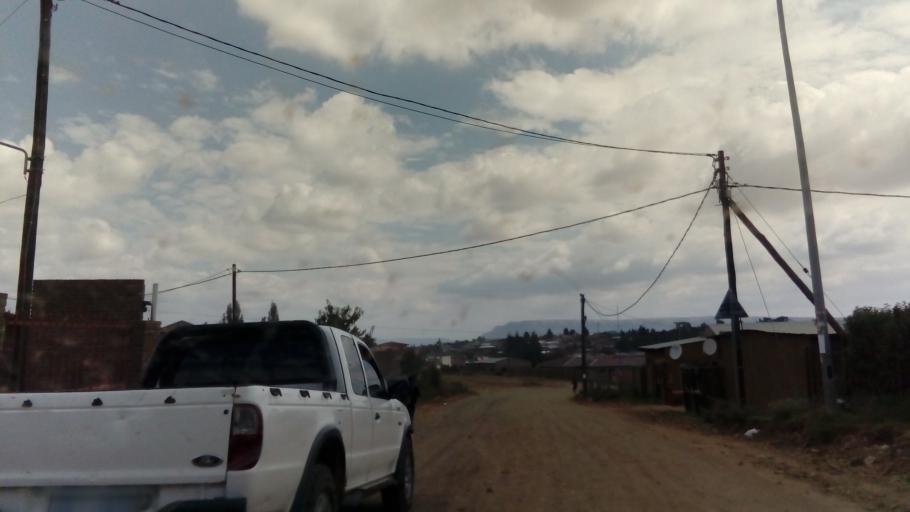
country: LS
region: Maseru
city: Maseru
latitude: -29.3693
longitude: 27.5358
